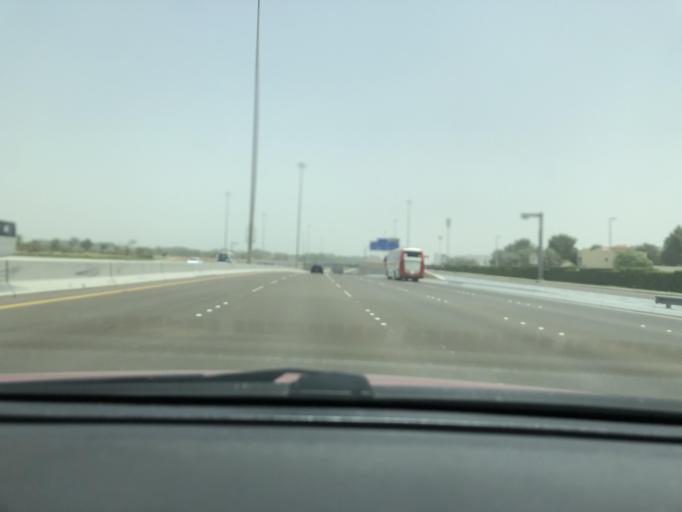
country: AE
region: Abu Dhabi
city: Abu Dhabi
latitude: 24.4395
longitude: 54.4548
